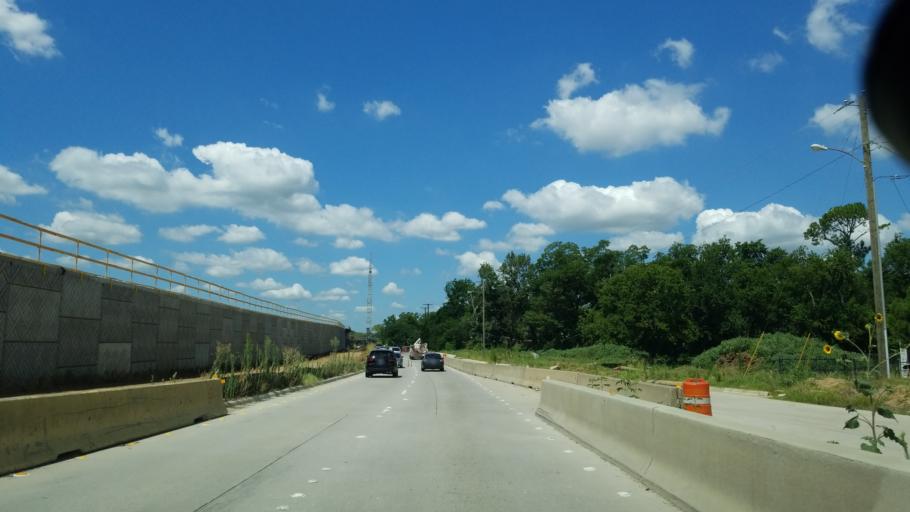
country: US
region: Texas
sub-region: Dallas County
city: Dallas
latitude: 32.7471
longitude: -96.7557
